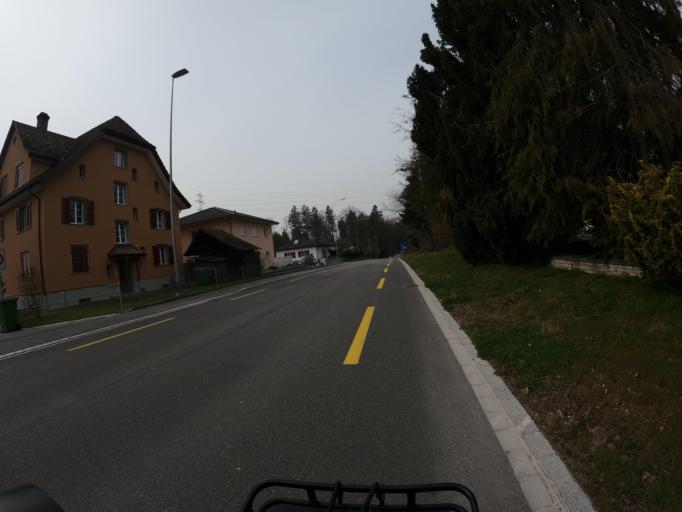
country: CH
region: Aargau
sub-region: Bezirk Brugg
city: Rupperswil
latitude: 47.4044
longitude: 8.1177
